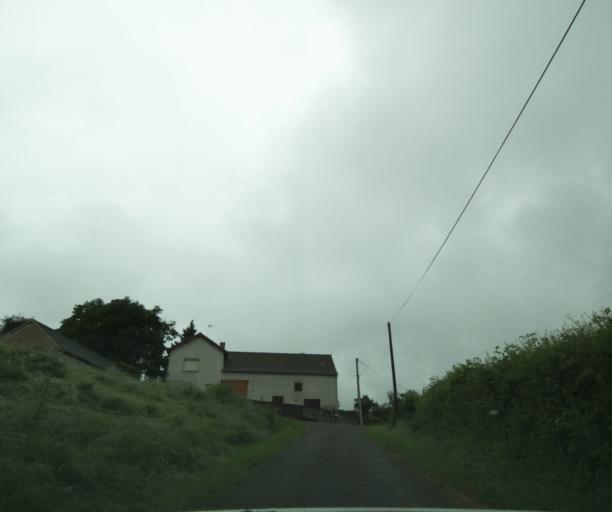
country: FR
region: Bourgogne
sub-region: Departement de Saone-et-Loire
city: Charolles
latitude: 46.4380
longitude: 4.3187
